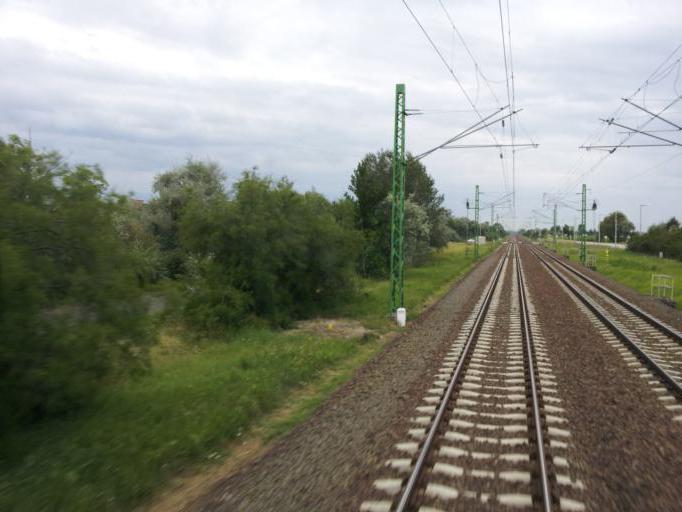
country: HU
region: Fejer
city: Gardony
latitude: 47.1892
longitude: 18.5854
